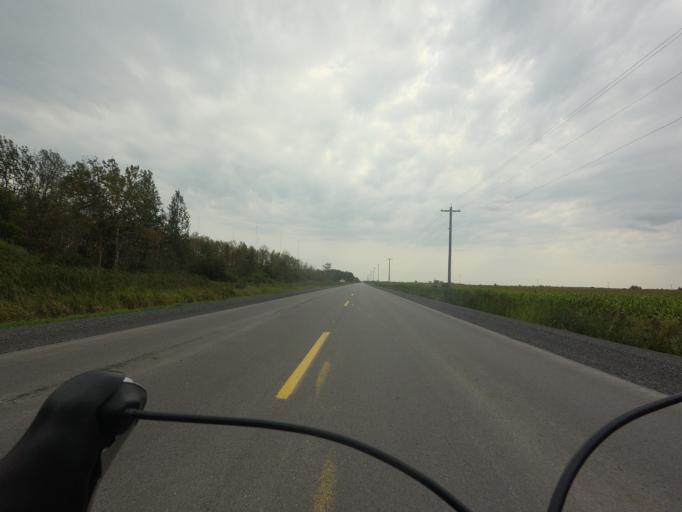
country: CA
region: Ontario
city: Bells Corners
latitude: 45.2191
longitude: -75.7735
